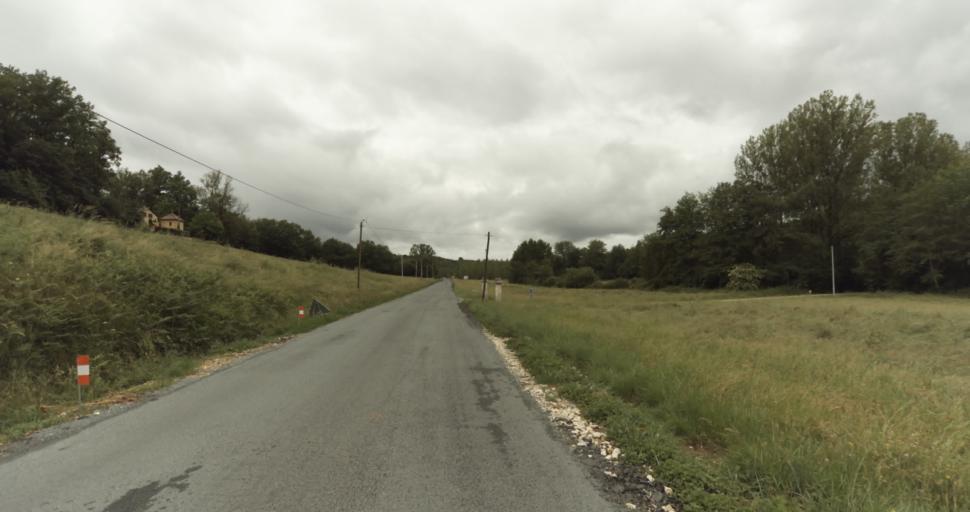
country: FR
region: Aquitaine
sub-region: Departement du Lot-et-Garonne
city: Villereal
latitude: 44.6571
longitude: 0.8638
